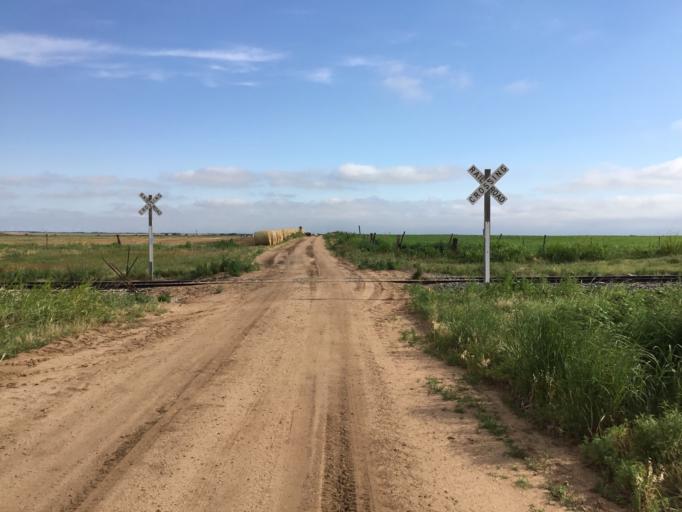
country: US
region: Kansas
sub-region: Kingman County
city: Kingman
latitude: 37.4439
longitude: -98.3277
